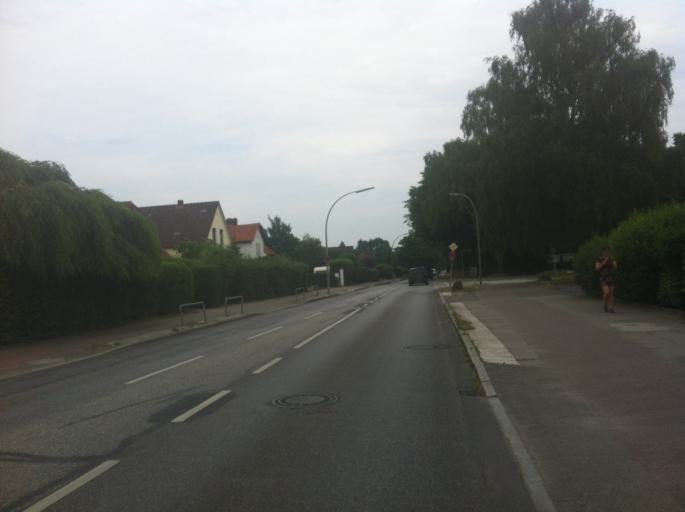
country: DE
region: Hamburg
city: Farmsen-Berne
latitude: 53.6076
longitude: 10.1367
